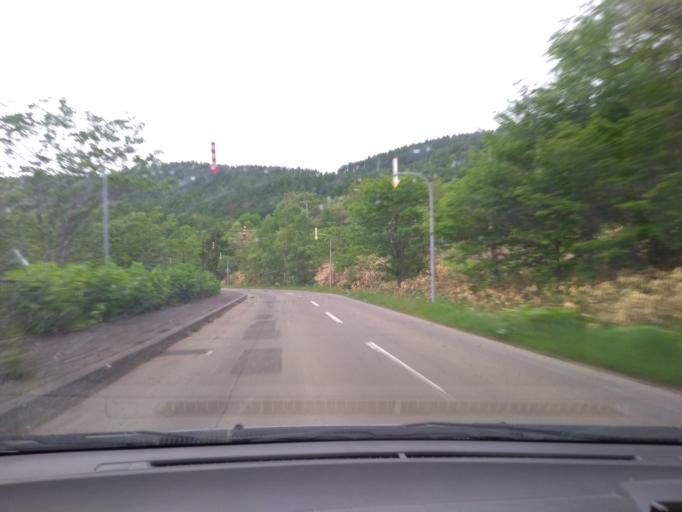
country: JP
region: Hokkaido
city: Shimo-furano
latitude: 43.1698
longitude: 142.5136
